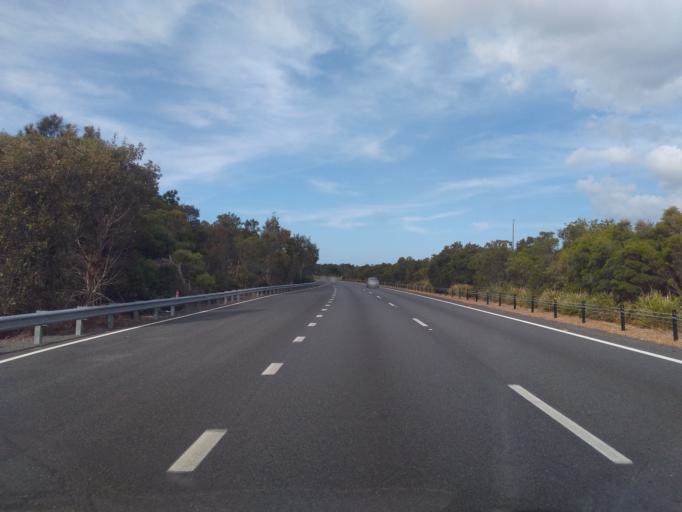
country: AU
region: Queensland
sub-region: Gold Coast
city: Tugun
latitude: -28.1701
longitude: 153.5026
